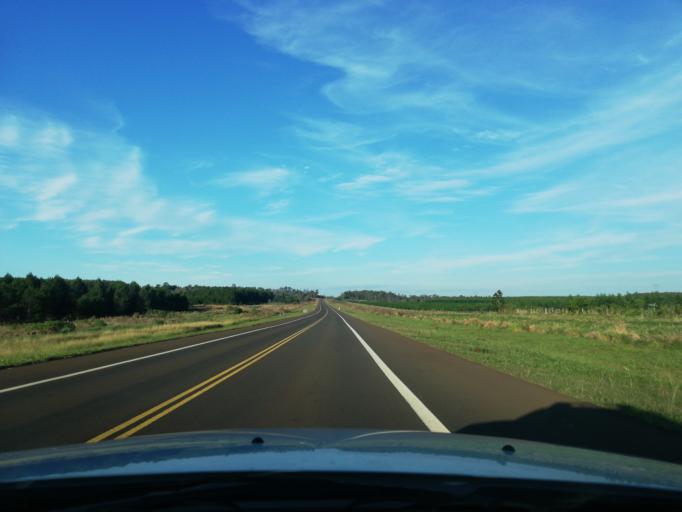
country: AR
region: Misiones
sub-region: Departamento de Capital
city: Posadas
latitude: -27.4599
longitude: -55.9998
